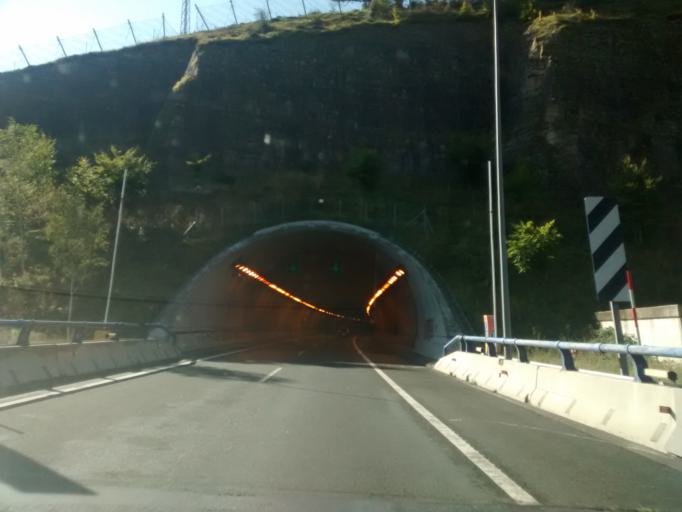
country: ES
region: Cantabria
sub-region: Provincia de Cantabria
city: Santiurde de Reinosa
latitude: 43.0527
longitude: -4.0867
